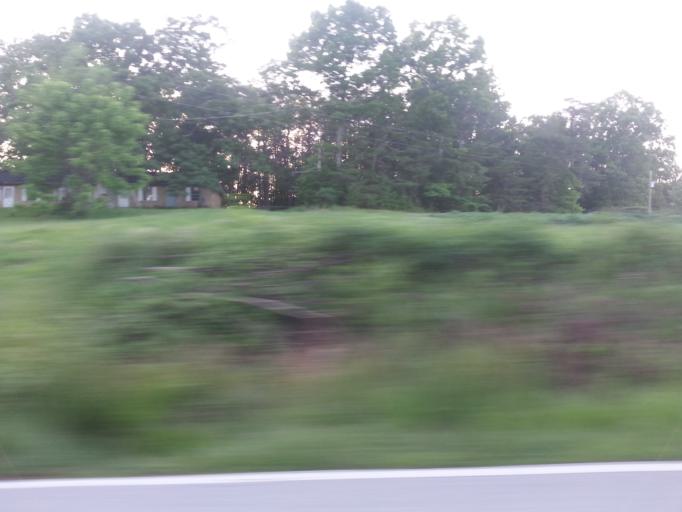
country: US
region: Tennessee
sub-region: McMinn County
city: Etowah
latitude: 35.2600
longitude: -84.2891
